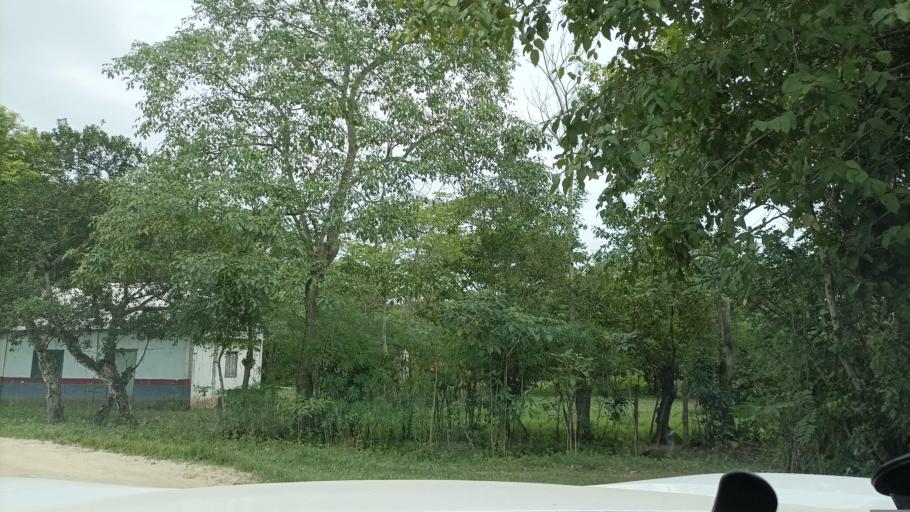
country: MX
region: Veracruz
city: Hidalgotitlan
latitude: 17.8059
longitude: -94.5419
